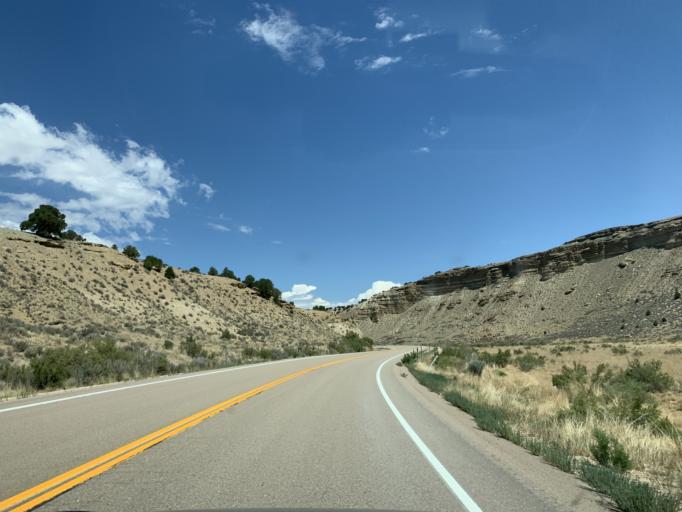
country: US
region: Utah
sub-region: Duchesne County
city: Duchesne
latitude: 39.9757
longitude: -110.1625
